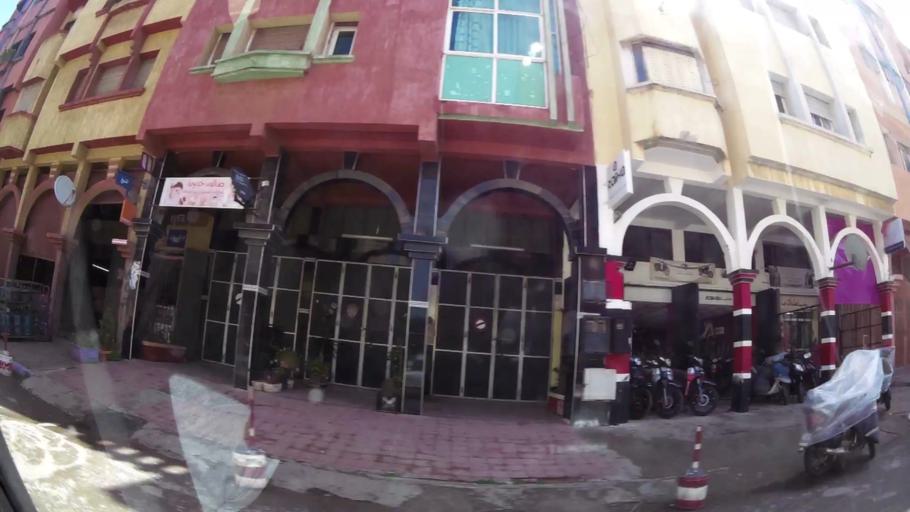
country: MA
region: Grand Casablanca
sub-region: Mohammedia
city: Mohammedia
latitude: 33.6386
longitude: -7.4529
